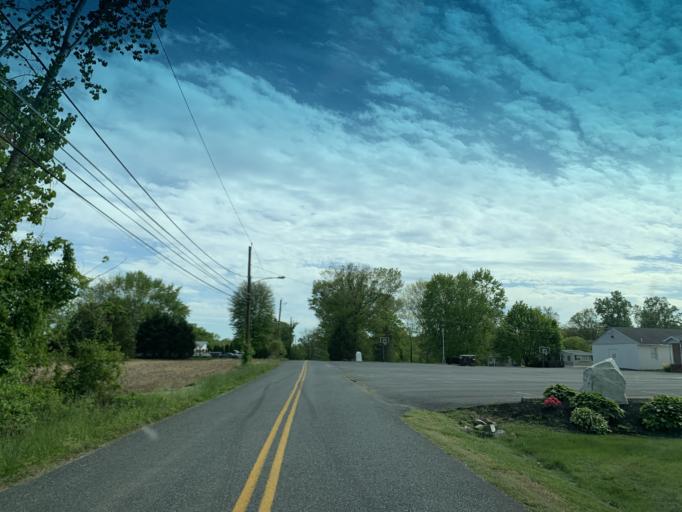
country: US
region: Maryland
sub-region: Harford County
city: Aberdeen
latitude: 39.6482
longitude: -76.2297
